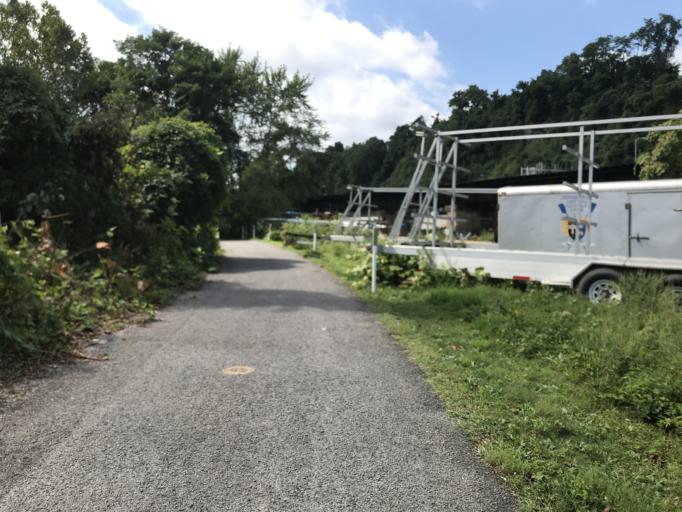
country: US
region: Pennsylvania
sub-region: Allegheny County
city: Millvale
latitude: 40.4696
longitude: -79.9748
